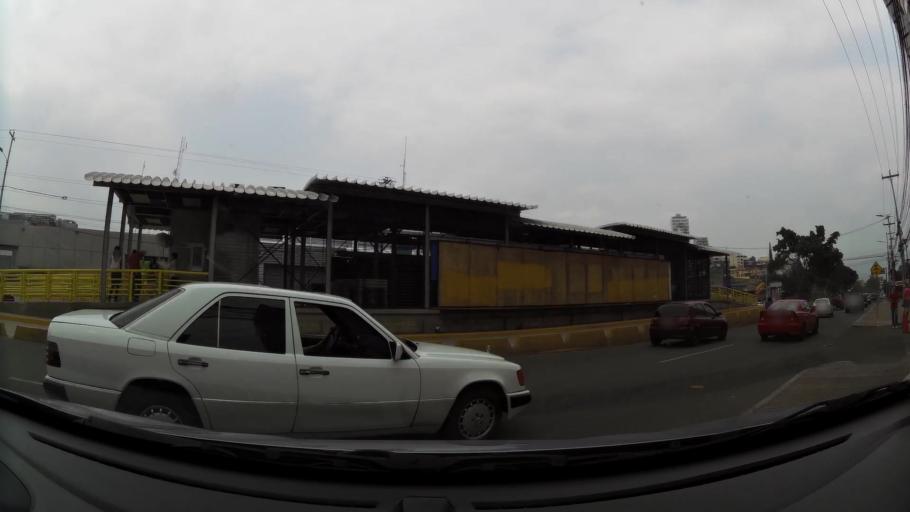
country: HN
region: Francisco Morazan
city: Tegucigalpa
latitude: 14.0855
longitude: -87.1859
